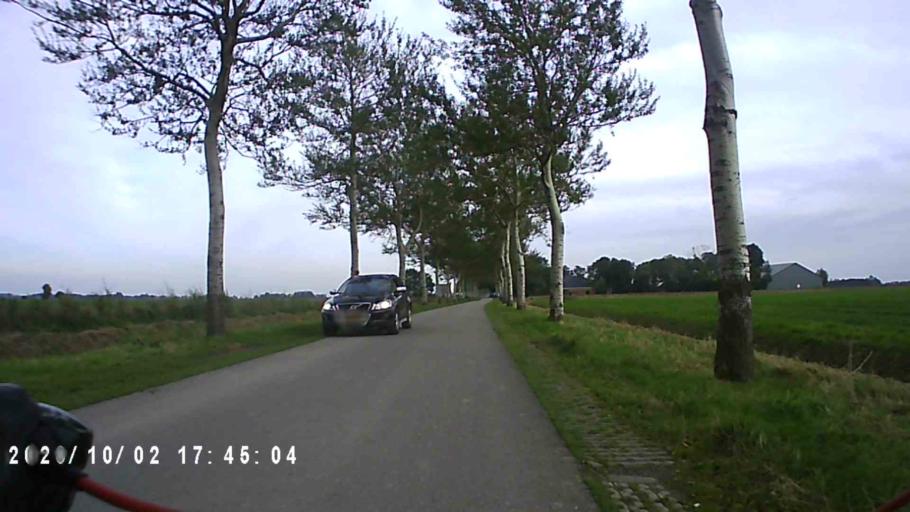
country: NL
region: Groningen
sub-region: Gemeente Zuidhorn
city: Oldehove
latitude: 53.3342
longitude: 6.3899
